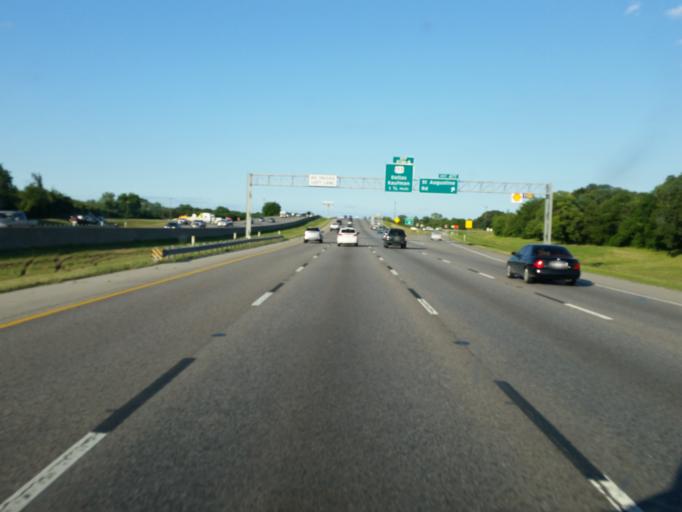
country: US
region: Texas
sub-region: Dallas County
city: Hutchins
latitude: 32.6817
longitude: -96.6620
